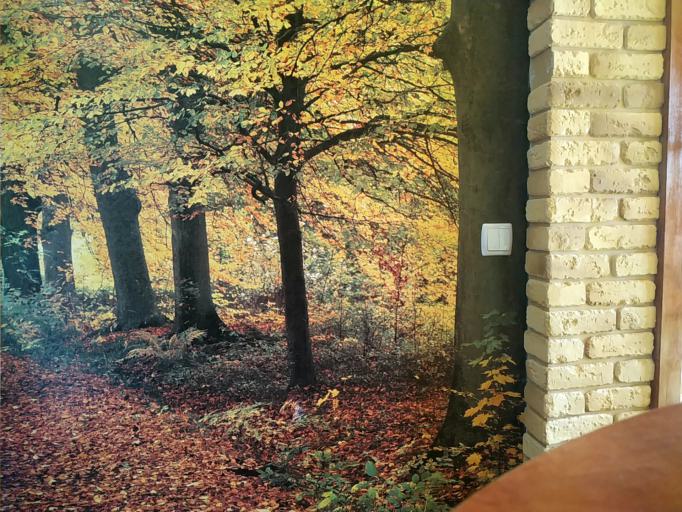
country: RU
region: Vologda
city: Molochnoye
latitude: 58.9412
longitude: 39.6577
